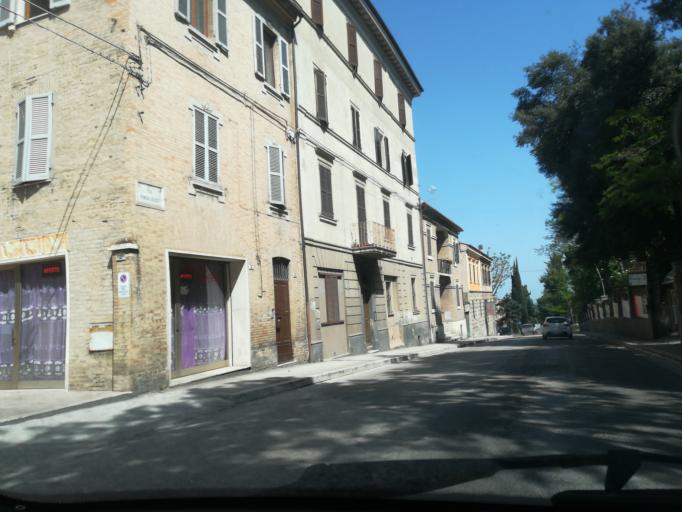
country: IT
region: The Marches
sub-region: Provincia di Macerata
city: Macerata
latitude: 43.2957
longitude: 13.4574
